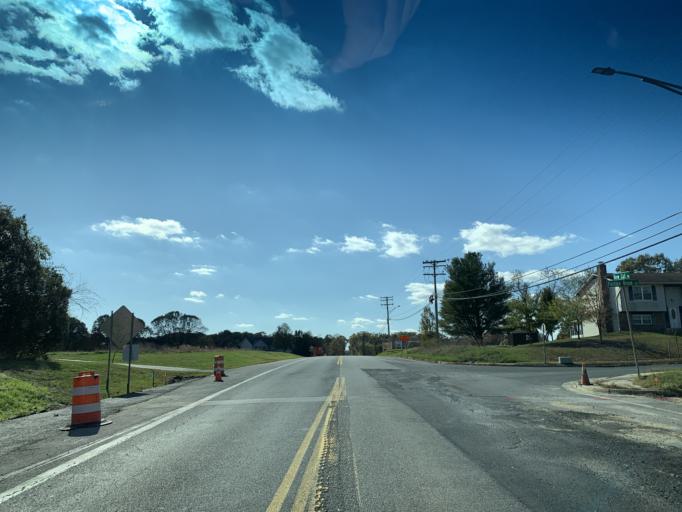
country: US
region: Maryland
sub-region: Anne Arundel County
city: South Gate
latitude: 39.1178
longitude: -76.6468
